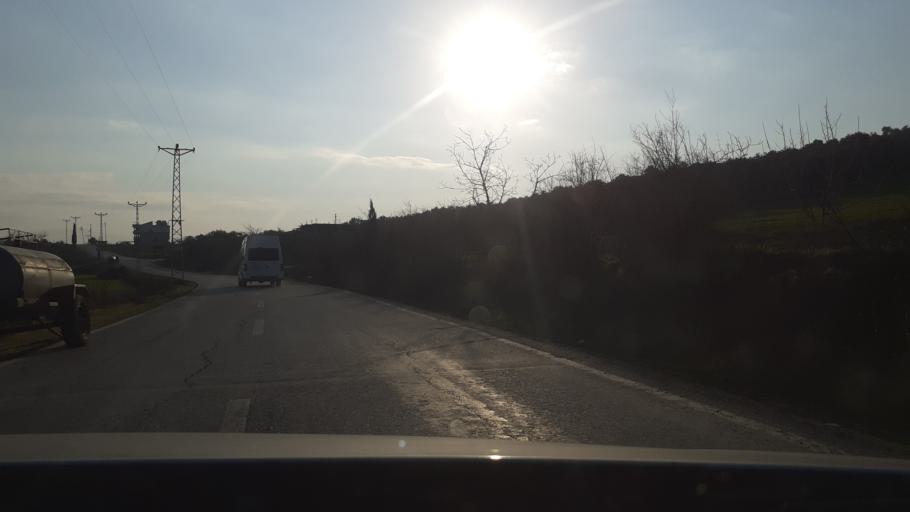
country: TR
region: Hatay
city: Boynuyogun
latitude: 36.1380
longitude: 36.3144
